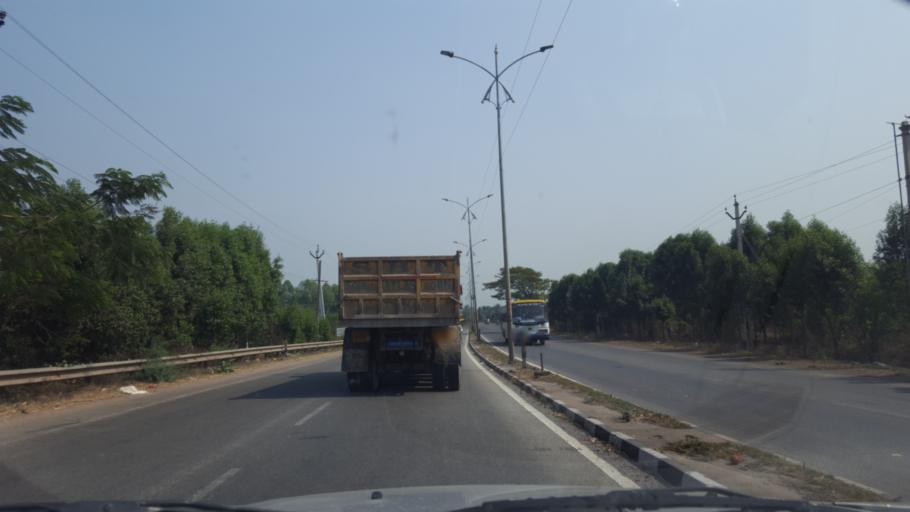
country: IN
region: Andhra Pradesh
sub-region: Vishakhapatnam
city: Anakapalle
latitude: 17.6891
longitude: 83.0754
